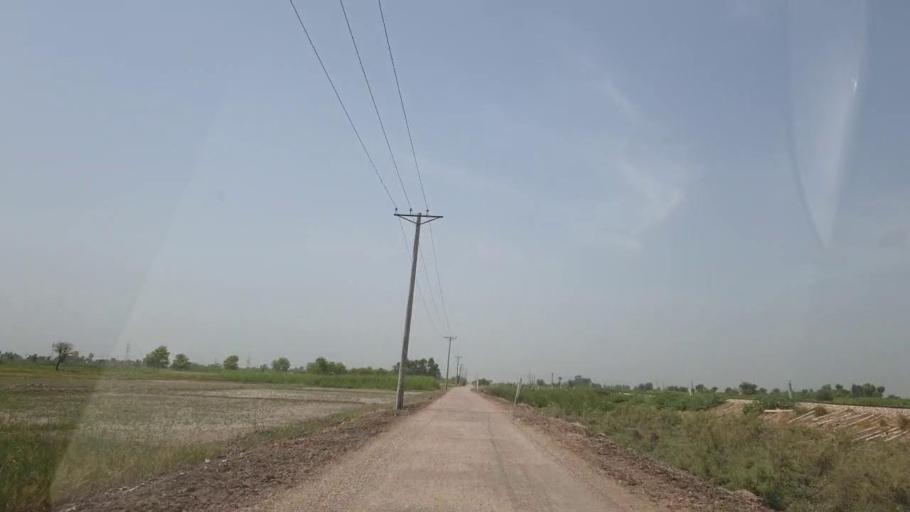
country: PK
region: Sindh
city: Gambat
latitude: 27.3238
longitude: 68.5379
